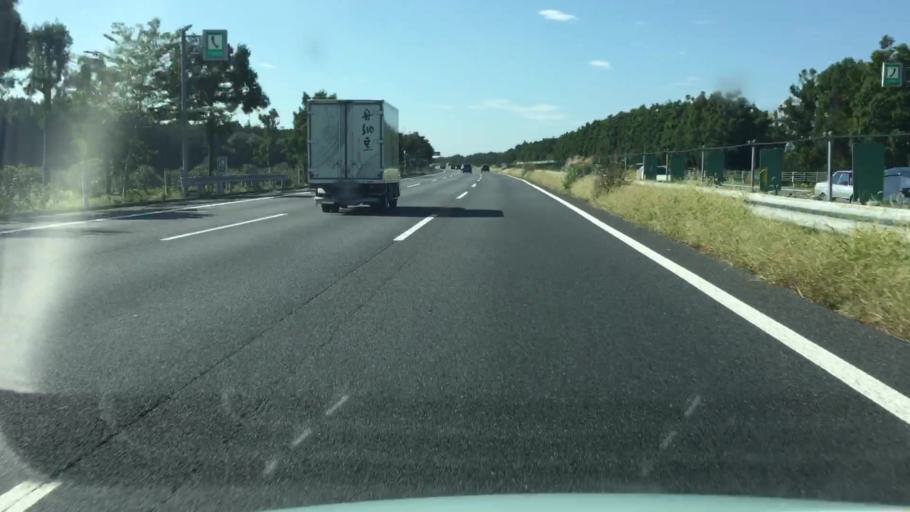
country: JP
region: Ibaraki
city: Tomobe
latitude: 36.2673
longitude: 140.3025
